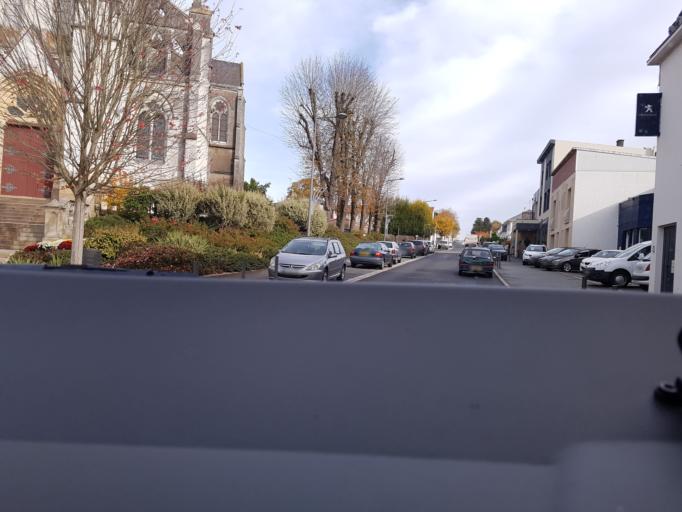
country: FR
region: Pays de la Loire
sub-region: Departement de Maine-et-Loire
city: Beaupreau
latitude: 47.2017
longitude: -0.9916
